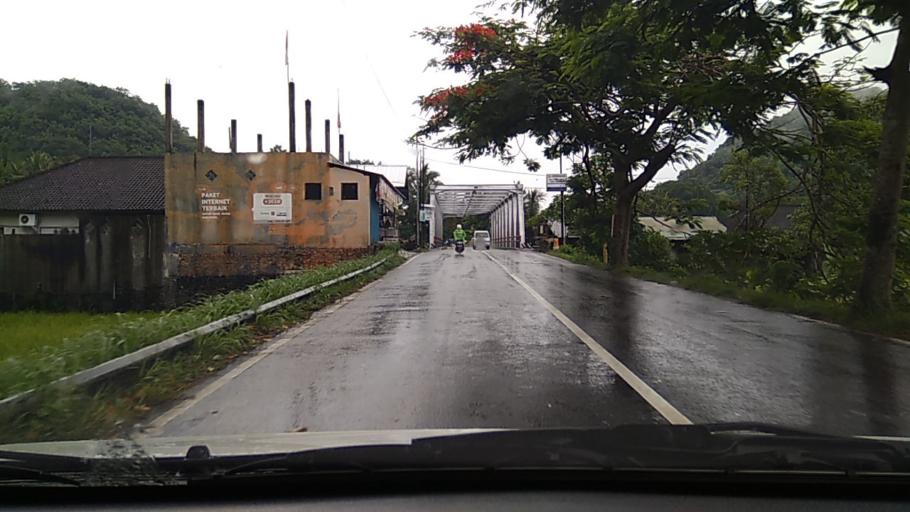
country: ID
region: Bali
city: Banjar Bugbug
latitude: -8.4925
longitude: 115.5890
